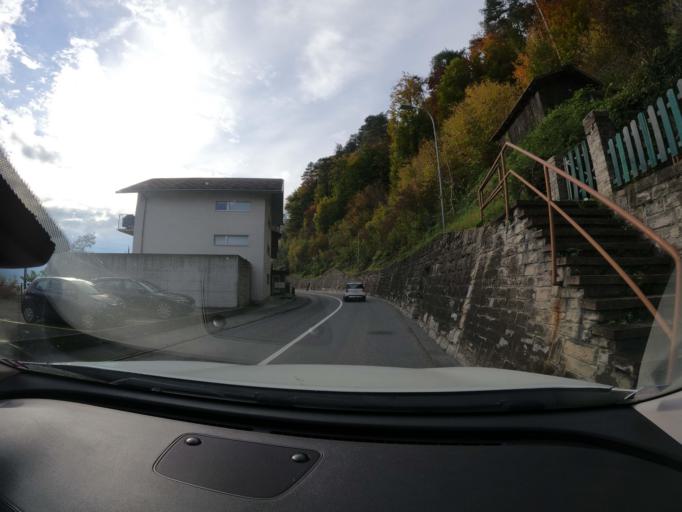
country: CH
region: Bern
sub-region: Interlaken-Oberhasli District
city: Brienz
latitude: 46.7551
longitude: 8.0419
